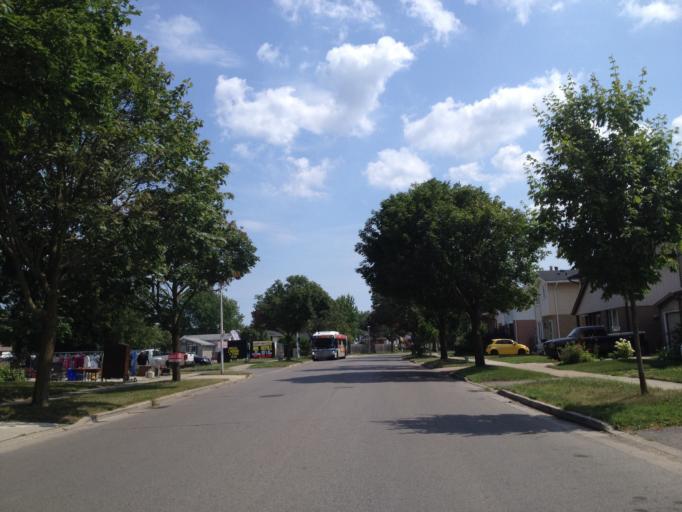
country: CA
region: Ontario
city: London
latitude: 43.0023
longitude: -81.3153
